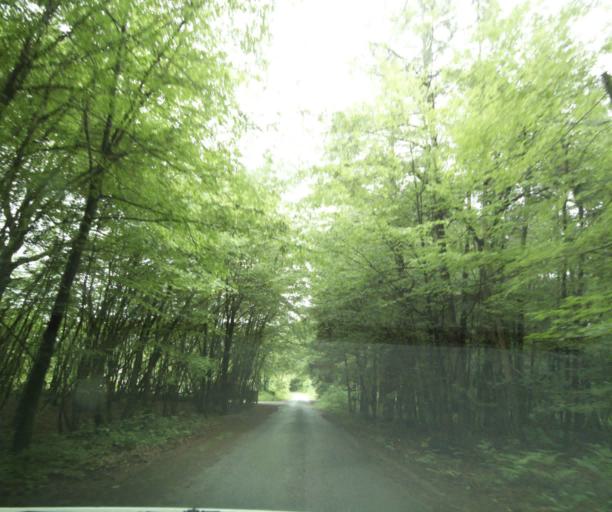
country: FR
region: Bourgogne
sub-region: Departement de Saone-et-Loire
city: Ciry-le-Noble
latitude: 46.5220
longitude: 4.3026
